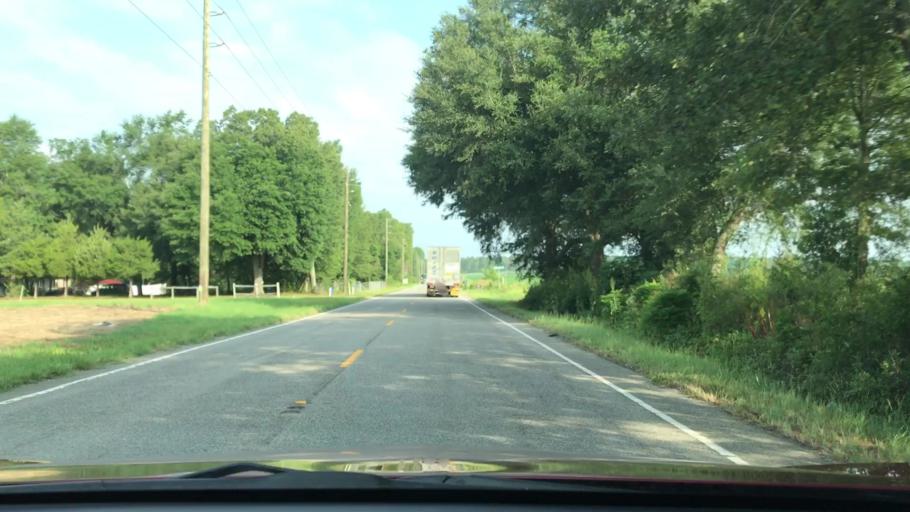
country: US
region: South Carolina
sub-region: Barnwell County
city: Blackville
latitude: 33.6096
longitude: -81.2739
